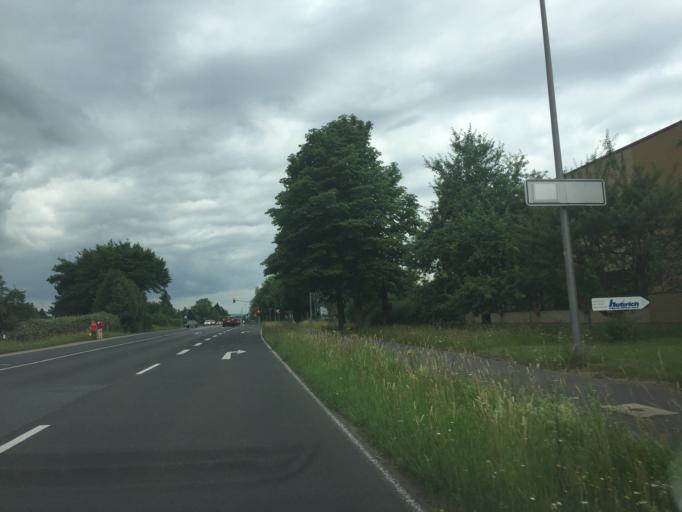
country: DE
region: Bavaria
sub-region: Regierungsbezirk Unterfranken
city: Aschaffenburg
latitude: 49.9639
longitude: 9.1309
